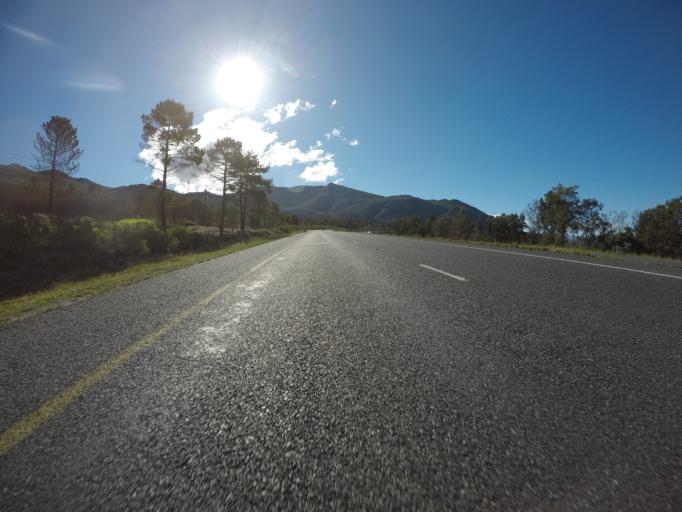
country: ZA
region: Western Cape
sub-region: Overberg District Municipality
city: Grabouw
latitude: -34.2241
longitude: 19.1877
